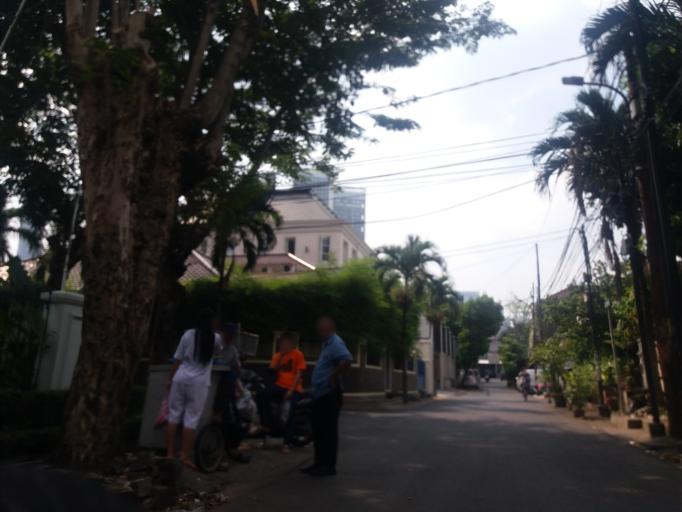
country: ID
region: Jakarta Raya
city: Jakarta
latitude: -6.2267
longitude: 106.8210
